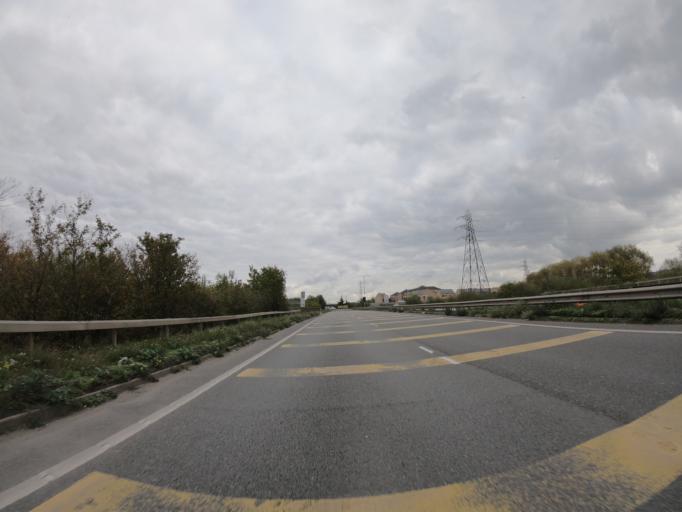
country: GB
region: England
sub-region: Kent
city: Dartford
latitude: 51.4592
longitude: 0.2175
